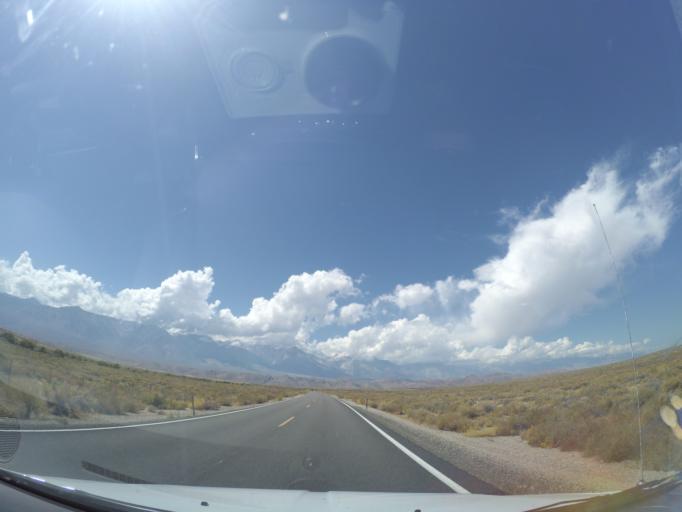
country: US
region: California
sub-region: Inyo County
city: Lone Pine
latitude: 36.5742
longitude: -117.9989
